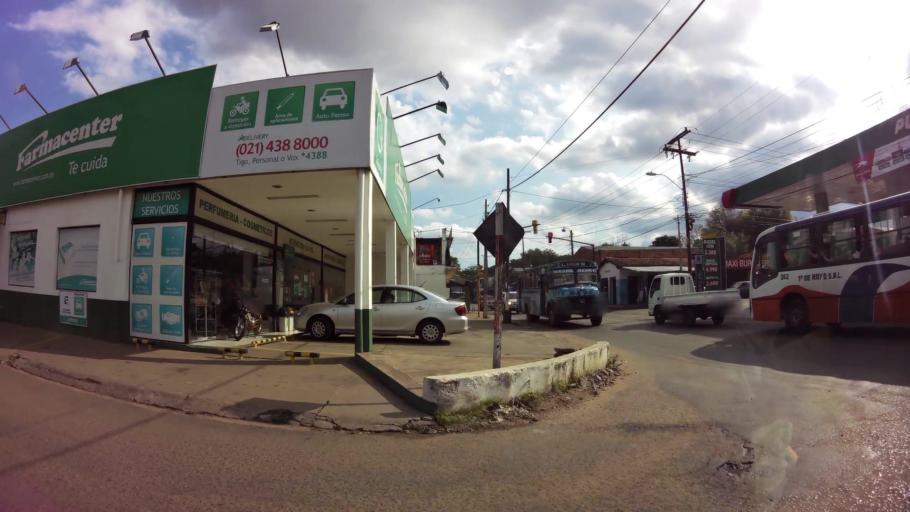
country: PY
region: Central
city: Fernando de la Mora
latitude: -25.3437
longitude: -57.5474
